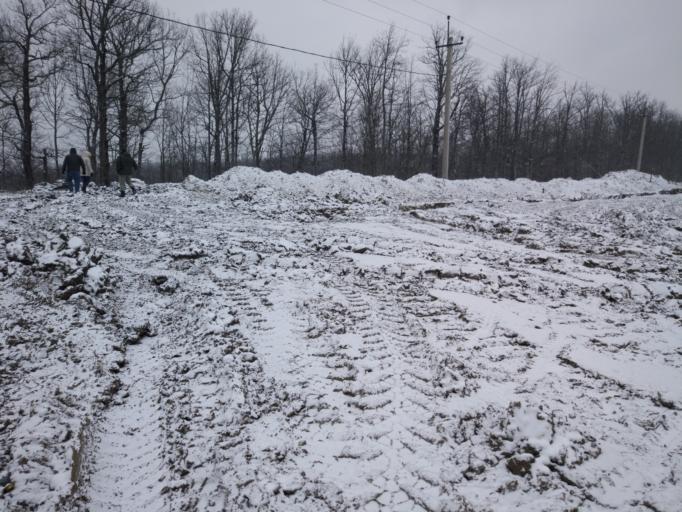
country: RU
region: Krasnodarskiy
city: Saratovskaya
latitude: 44.6174
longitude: 39.2362
